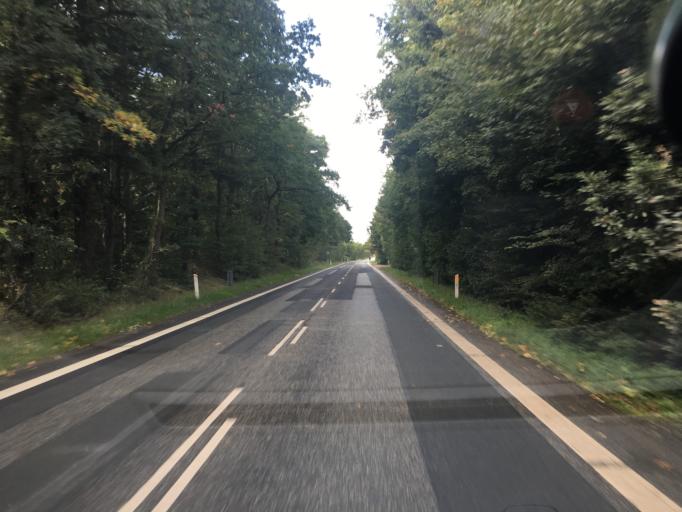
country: DK
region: South Denmark
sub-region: Tonder Kommune
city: Tonder
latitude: 55.0094
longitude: 8.8001
